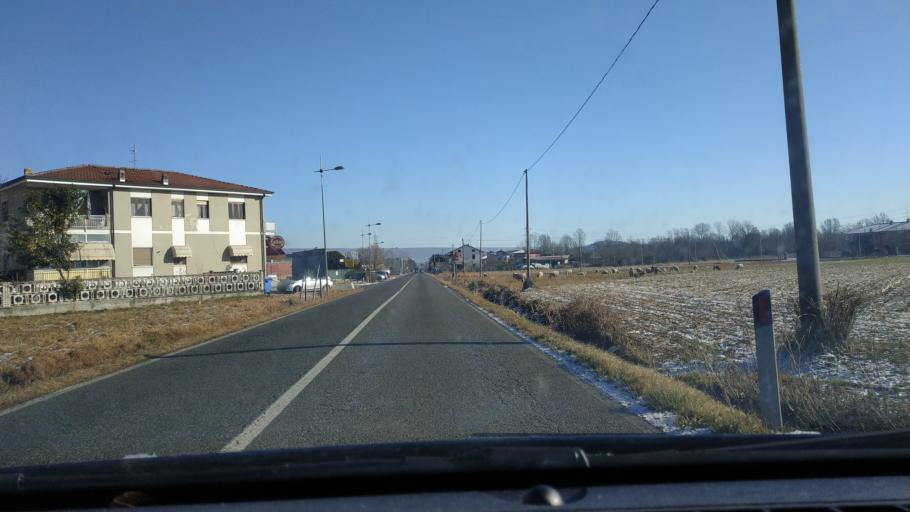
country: IT
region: Piedmont
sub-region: Provincia di Torino
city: Loranze
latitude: 45.4390
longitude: 7.8106
